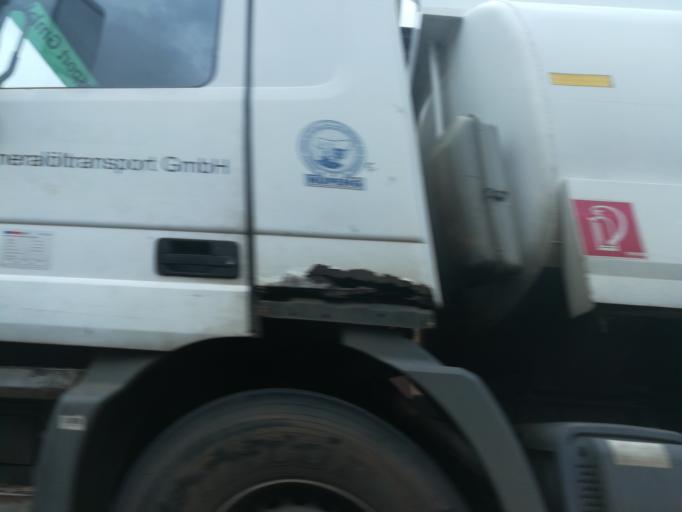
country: NG
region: Lagos
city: Ojota
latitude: 6.5699
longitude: 3.3725
